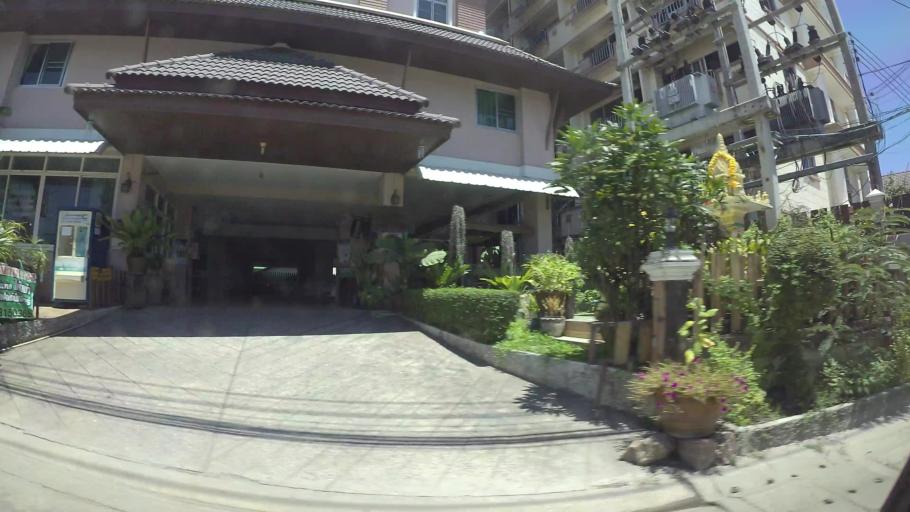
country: TH
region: Chon Buri
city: Si Racha
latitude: 13.1134
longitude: 100.9294
